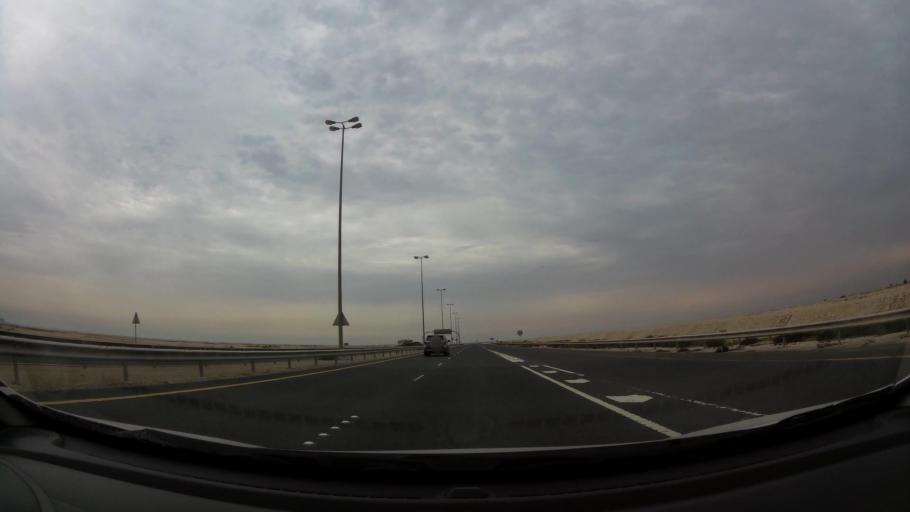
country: BH
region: Central Governorate
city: Dar Kulayb
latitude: 25.8824
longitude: 50.5771
